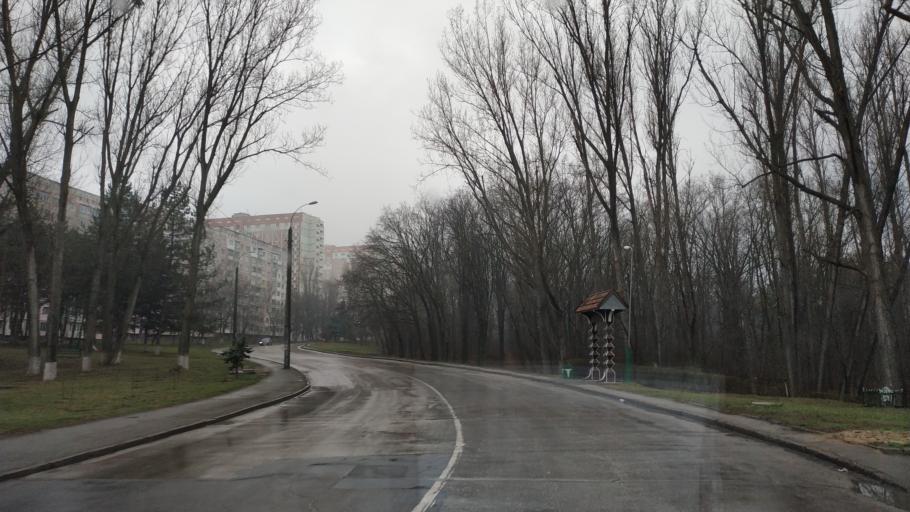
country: MD
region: Chisinau
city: Vatra
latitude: 47.0393
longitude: 28.7798
